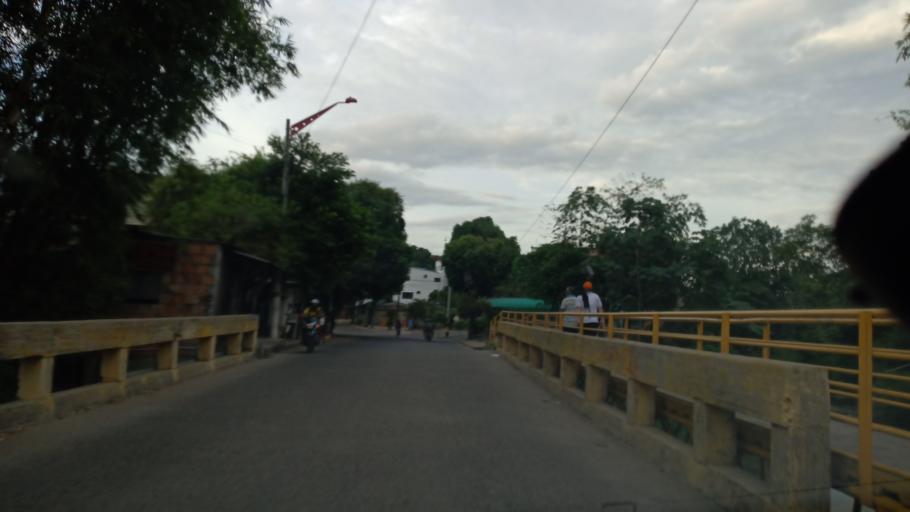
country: CO
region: Tolima
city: Melgar
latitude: 4.2028
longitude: -74.6461
